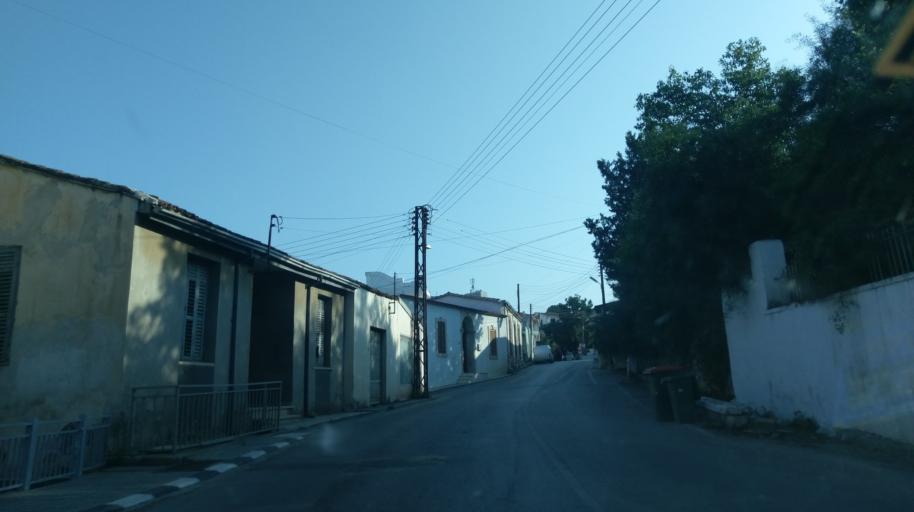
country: CY
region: Lefkosia
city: Lefka
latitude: 35.1148
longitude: 32.8489
